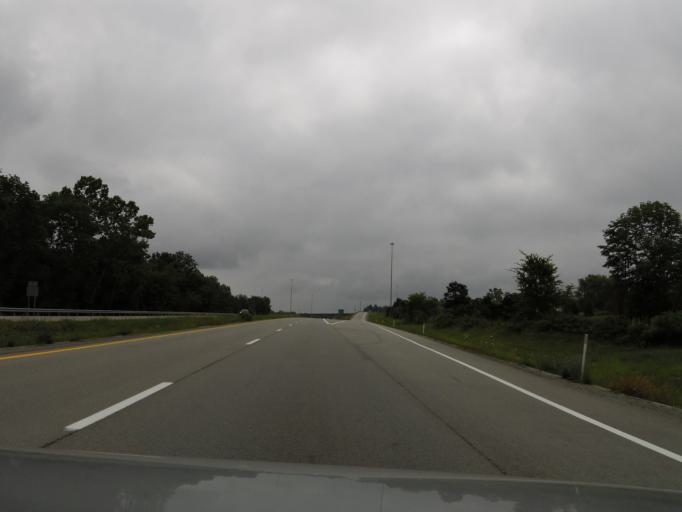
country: US
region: Kentucky
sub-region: Grayson County
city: Leitchfield
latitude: 37.4132
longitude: -86.5096
